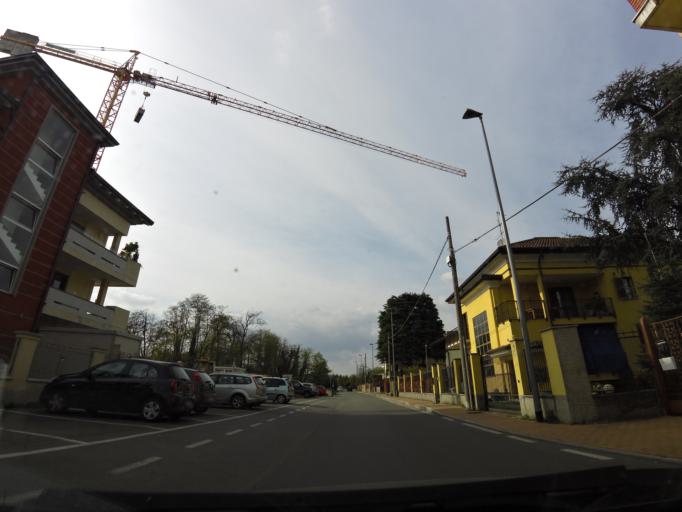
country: IT
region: Lombardy
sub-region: Citta metropolitana di Milano
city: Civesio
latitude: 45.3935
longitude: 9.2663
